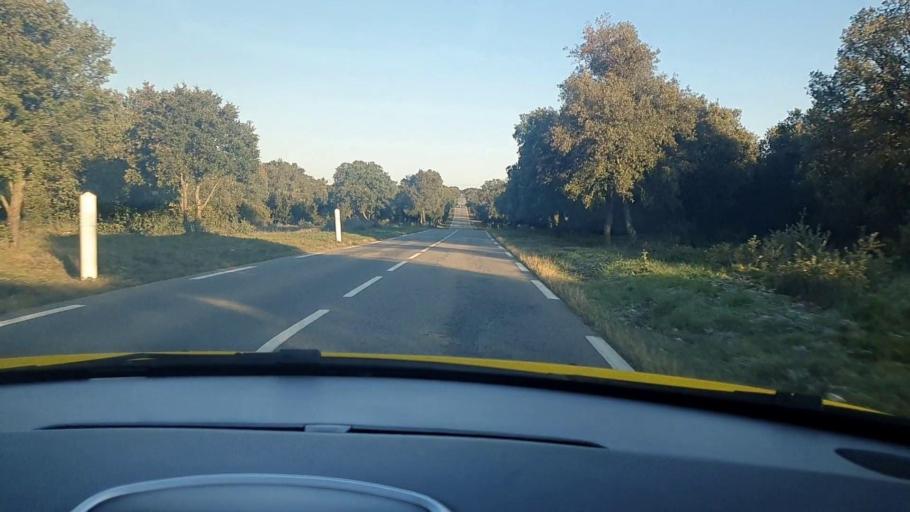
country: FR
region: Languedoc-Roussillon
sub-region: Departement du Gard
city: Montaren-et-Saint-Mediers
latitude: 44.0908
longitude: 4.3891
